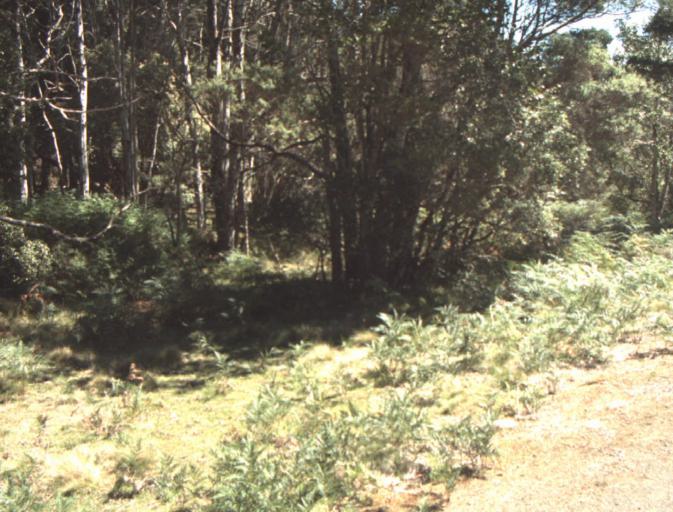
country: AU
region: Tasmania
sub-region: Dorset
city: Scottsdale
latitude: -41.3677
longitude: 147.4306
